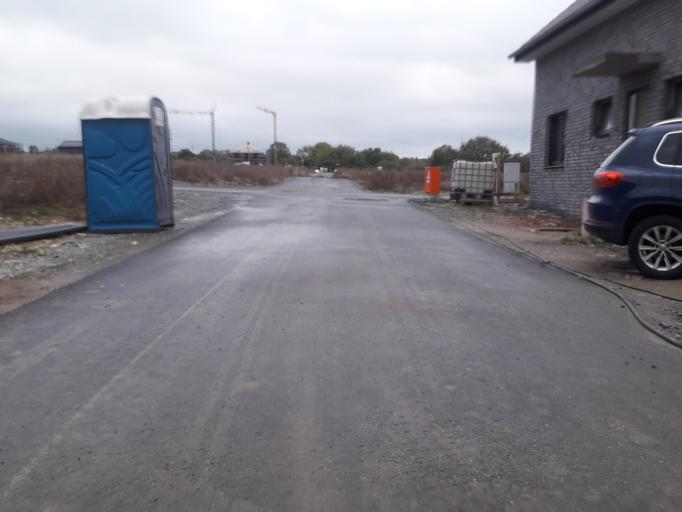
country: DE
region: North Rhine-Westphalia
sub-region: Regierungsbezirk Detmold
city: Paderborn
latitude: 51.7179
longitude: 8.8063
